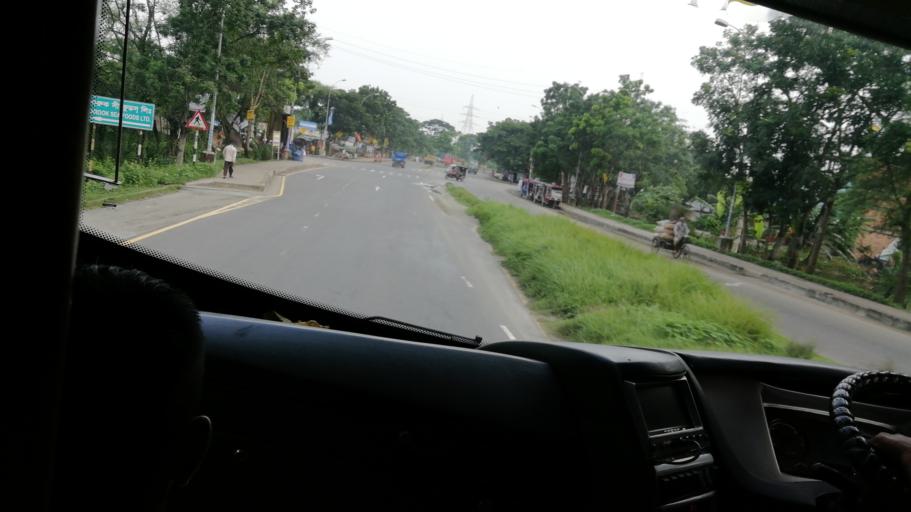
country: BD
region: Khulna
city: Khulna
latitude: 22.7858
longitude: 89.5377
